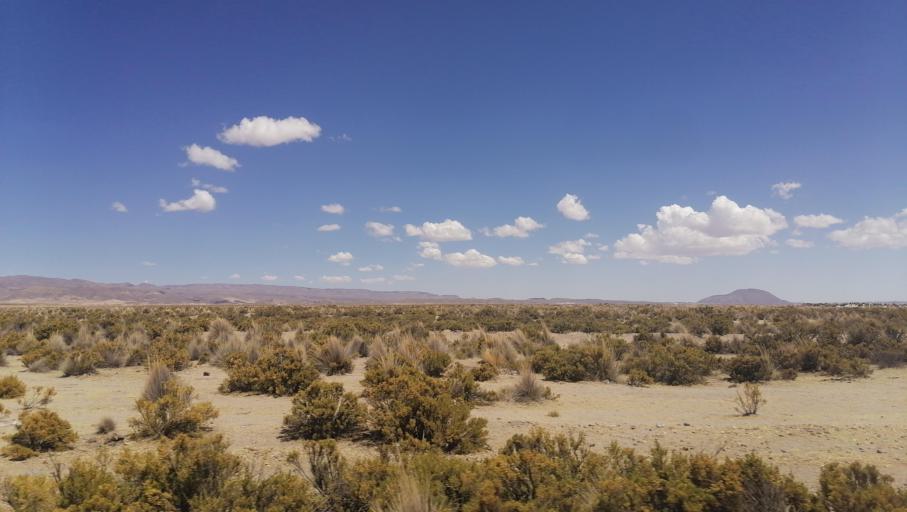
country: BO
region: Oruro
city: Challapata
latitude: -19.1708
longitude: -66.7887
